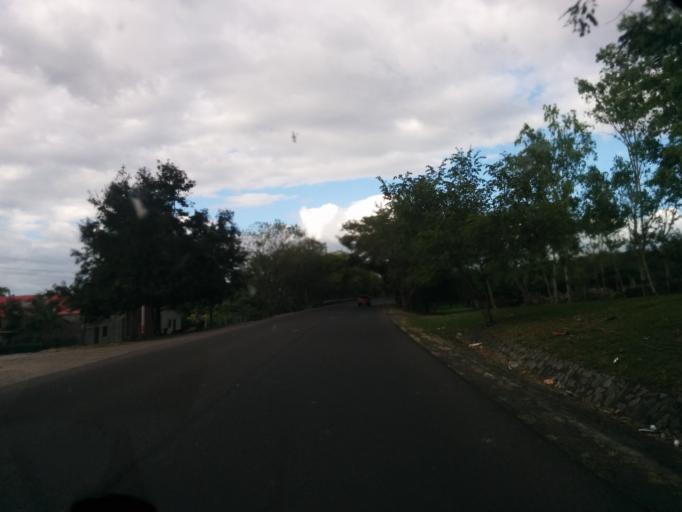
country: NI
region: Esteli
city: Esteli
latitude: 13.1557
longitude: -86.3702
